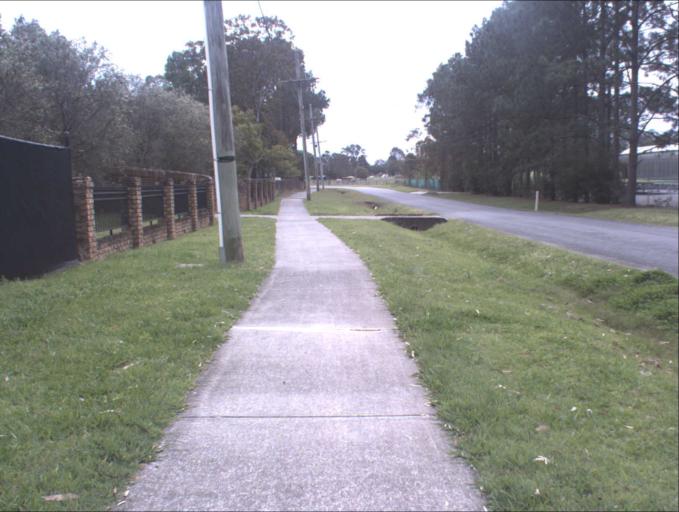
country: AU
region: Queensland
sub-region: Logan
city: Waterford West
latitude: -27.7003
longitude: 153.1387
